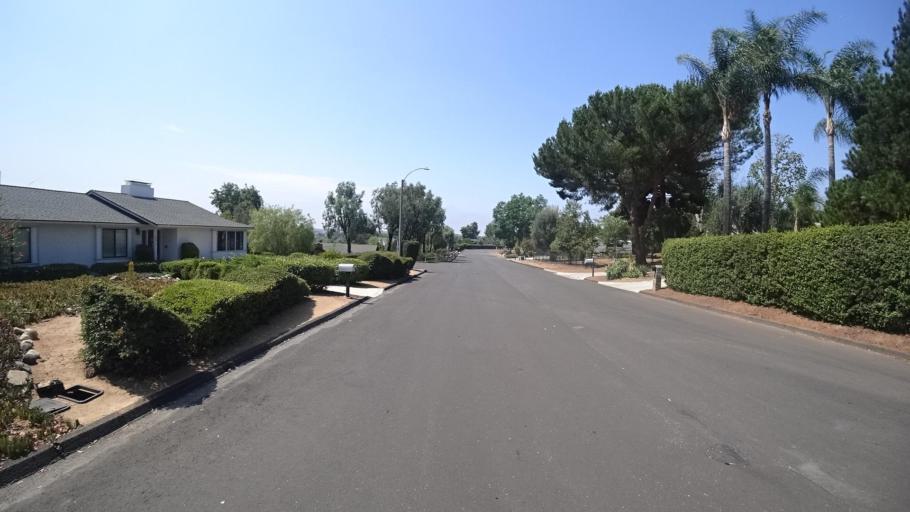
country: US
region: California
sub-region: San Diego County
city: Fallbrook
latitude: 33.3639
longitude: -117.2378
